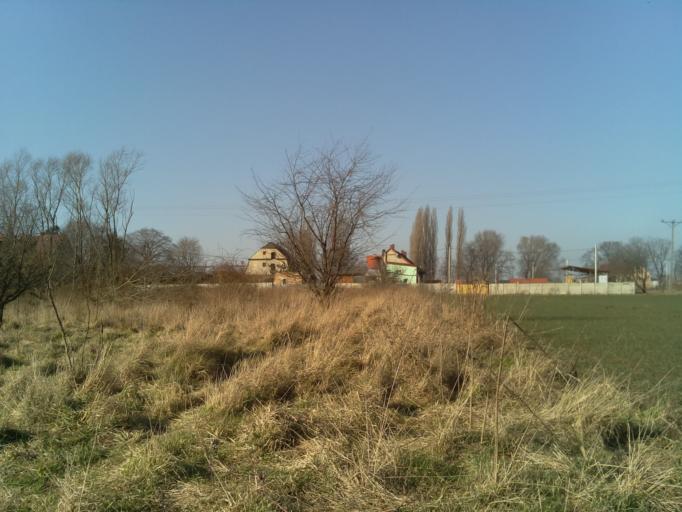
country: PL
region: Lower Silesian Voivodeship
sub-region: Powiat swidnicki
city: Swiebodzice
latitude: 50.8675
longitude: 16.3363
